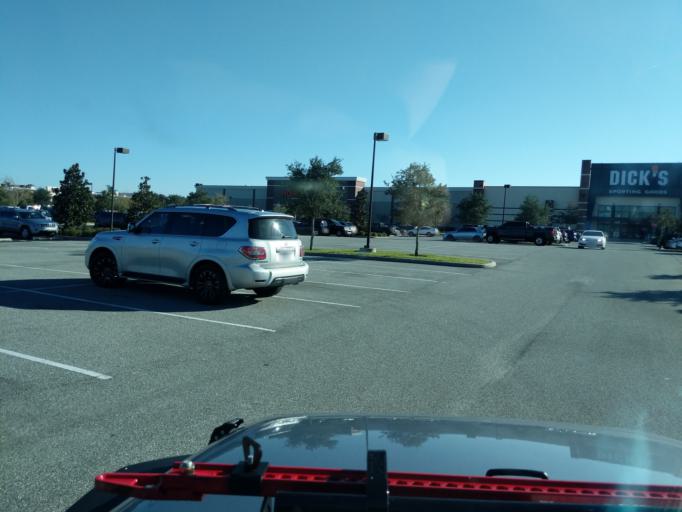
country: US
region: Florida
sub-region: Lake County
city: Minneola
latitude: 28.5452
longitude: -81.7333
